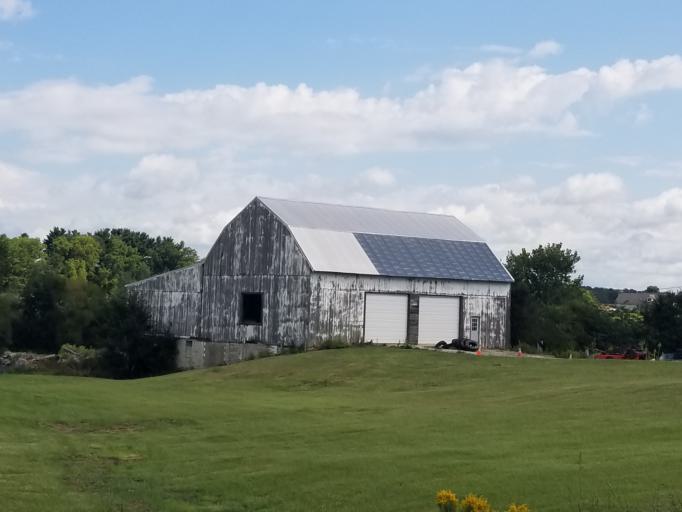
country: US
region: Ohio
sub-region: Seneca County
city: Tiffin
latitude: 41.0661
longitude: -83.0996
